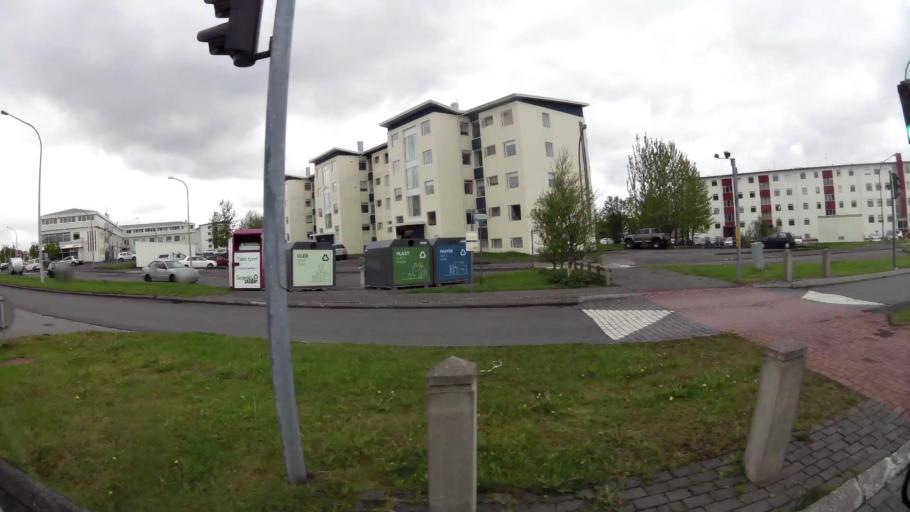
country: IS
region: Capital Region
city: Reykjavik
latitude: 64.1338
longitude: -21.8832
